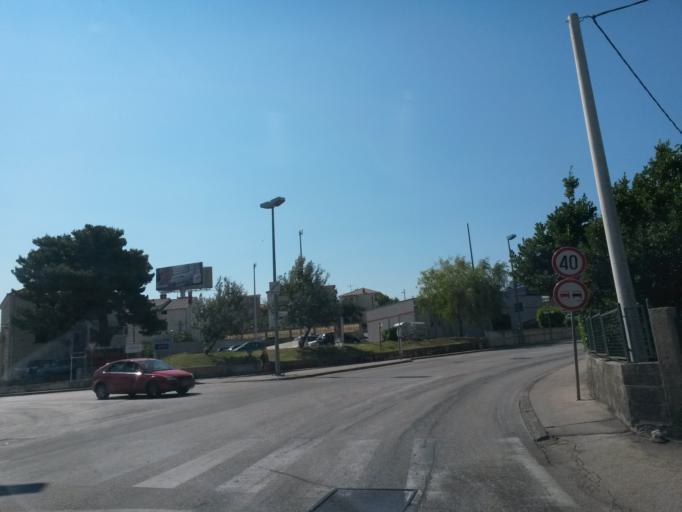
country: HR
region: Splitsko-Dalmatinska
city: Solin
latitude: 43.5329
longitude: 16.4867
